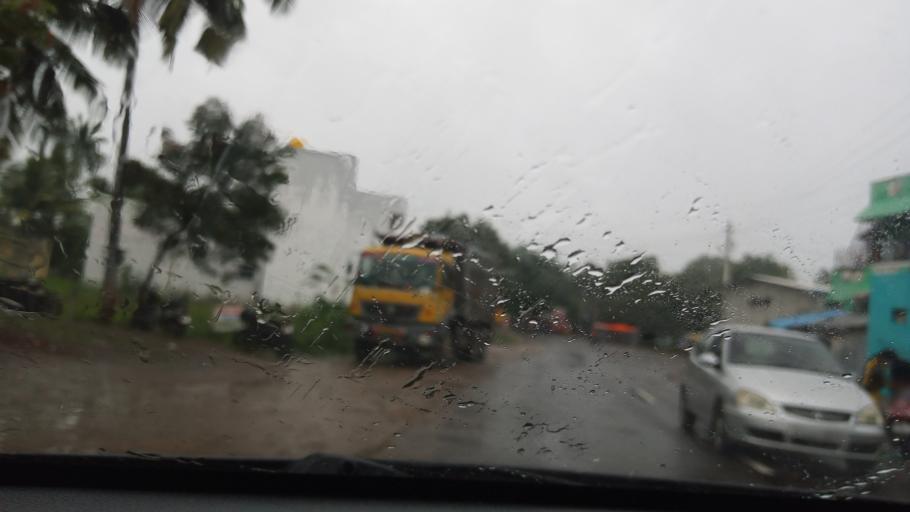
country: IN
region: Tamil Nadu
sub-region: Tiruvannamalai
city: Cheyyar
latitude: 12.6759
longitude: 79.5363
